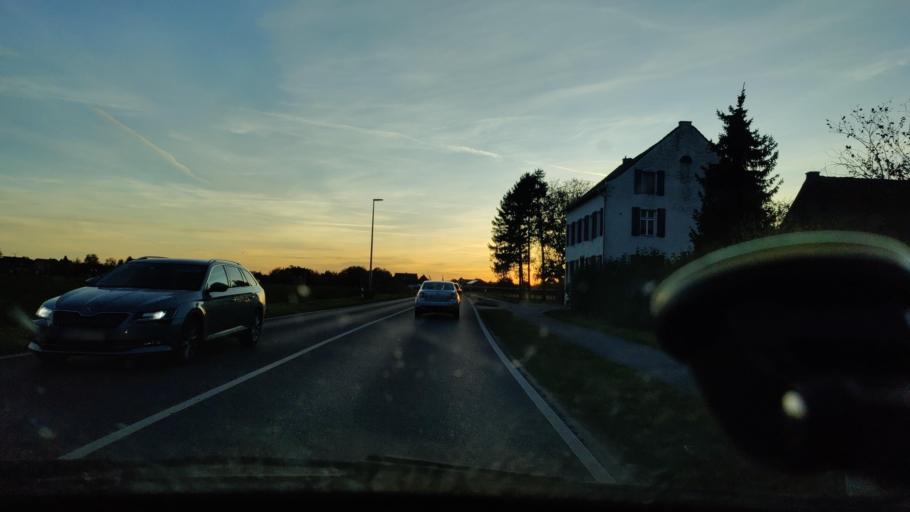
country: DE
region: North Rhine-Westphalia
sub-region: Regierungsbezirk Koln
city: Wassenberg
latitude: 51.0796
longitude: 6.1408
